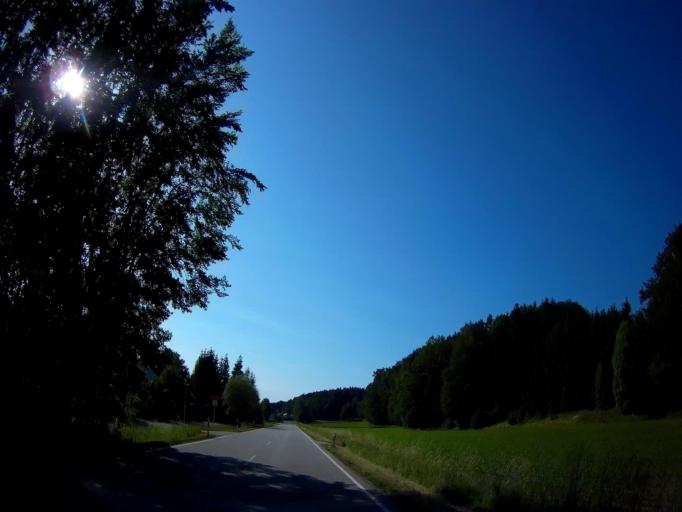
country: DE
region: Bavaria
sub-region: Upper Bavaria
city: Stammham
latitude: 48.2634
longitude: 12.8957
